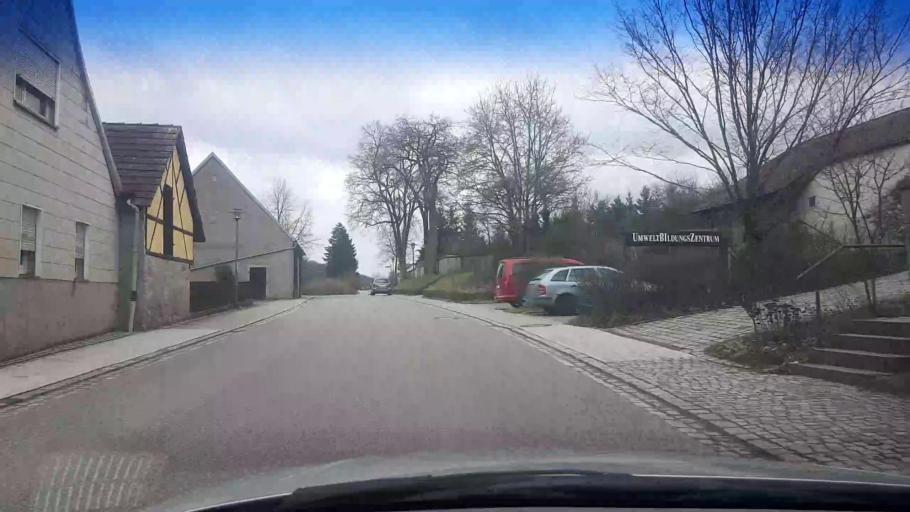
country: DE
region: Bavaria
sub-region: Regierungsbezirk Unterfranken
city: Sand
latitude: 49.9482
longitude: 10.5973
